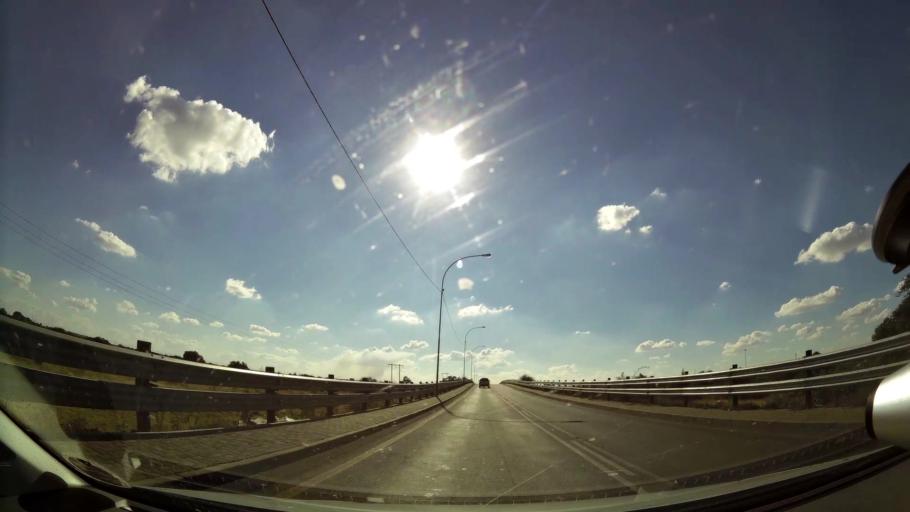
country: ZA
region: Northern Cape
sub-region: Frances Baard District Municipality
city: Kimberley
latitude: -28.7805
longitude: 24.7674
